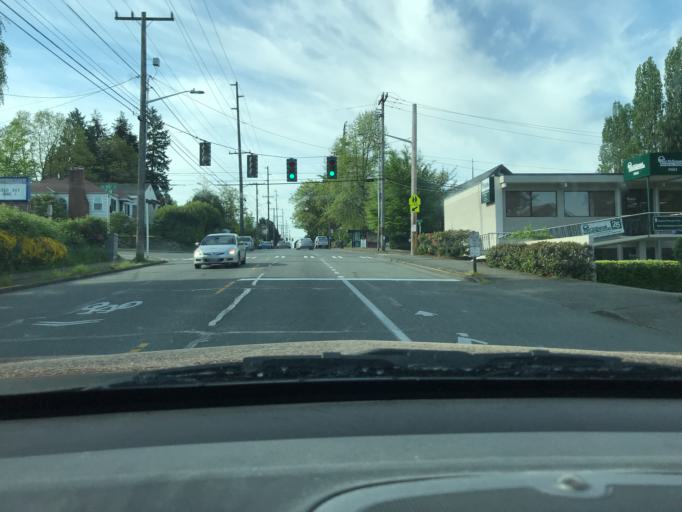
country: US
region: Washington
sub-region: King County
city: Shoreline
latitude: 47.6982
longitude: -122.3231
